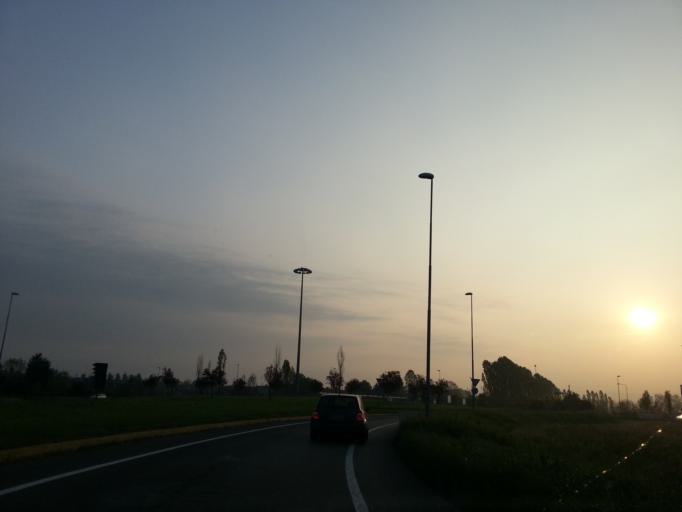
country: IT
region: Emilia-Romagna
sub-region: Provincia di Reggio Emilia
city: Fogliano
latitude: 44.6761
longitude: 10.6644
